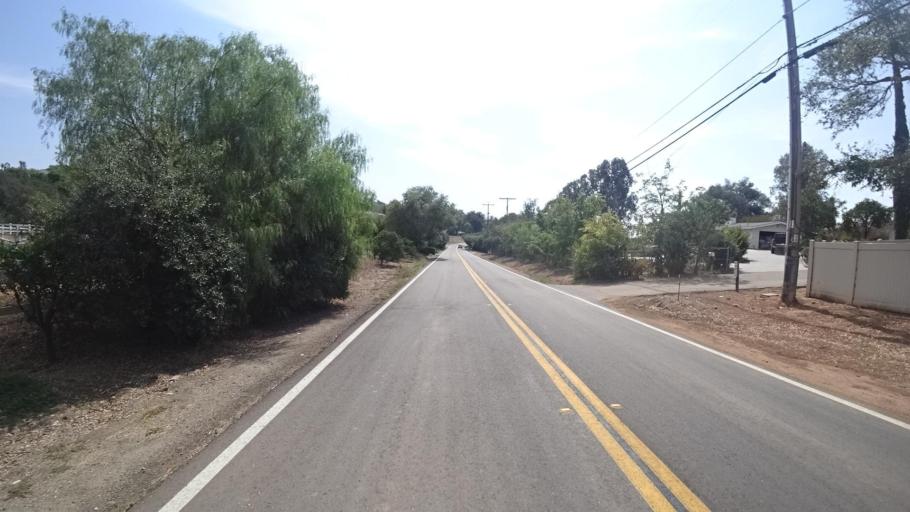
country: US
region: California
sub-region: San Diego County
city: Escondido
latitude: 33.1043
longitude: -117.0451
